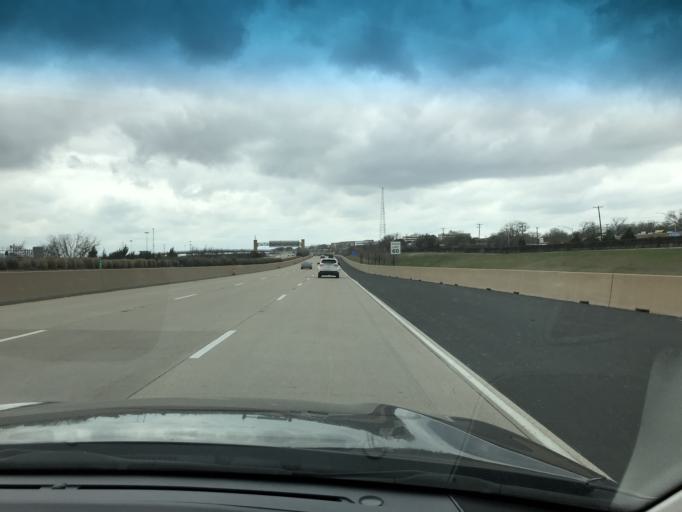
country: US
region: Texas
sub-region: Tarrant County
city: Westworth
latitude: 32.7259
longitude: -97.3774
